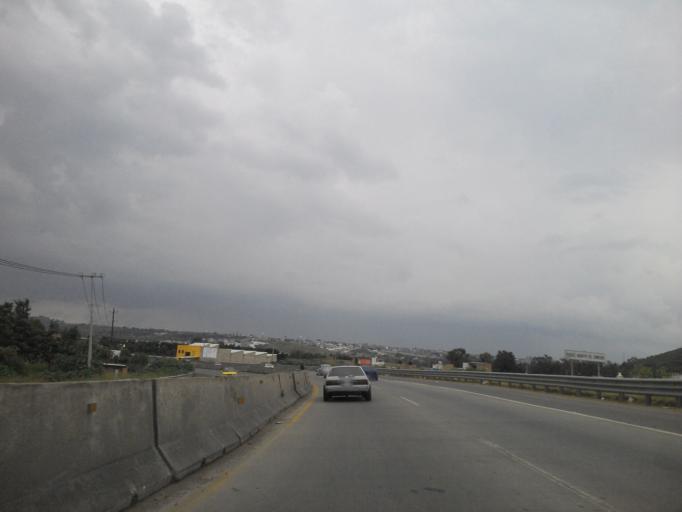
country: MX
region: Jalisco
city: Tonala
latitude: 20.5972
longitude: -103.2285
